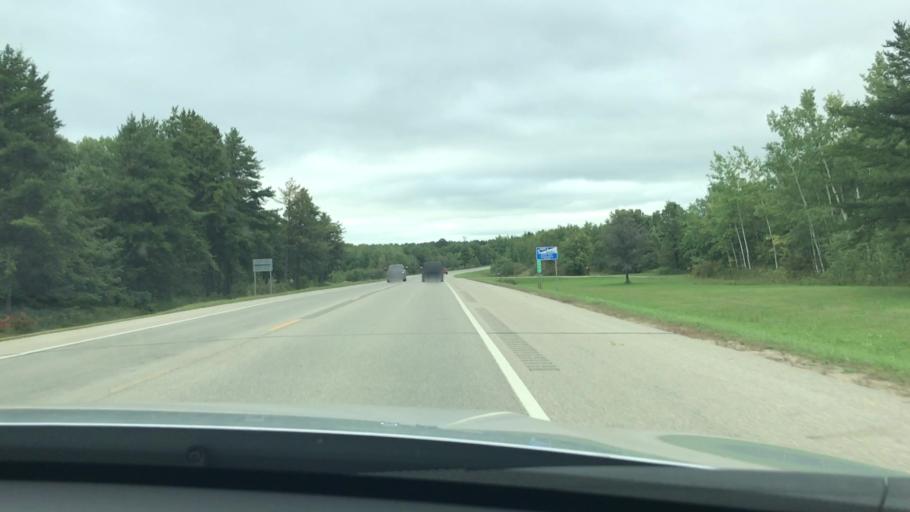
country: US
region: Minnesota
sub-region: Wadena County
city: Menahga
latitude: 46.8393
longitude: -95.0855
